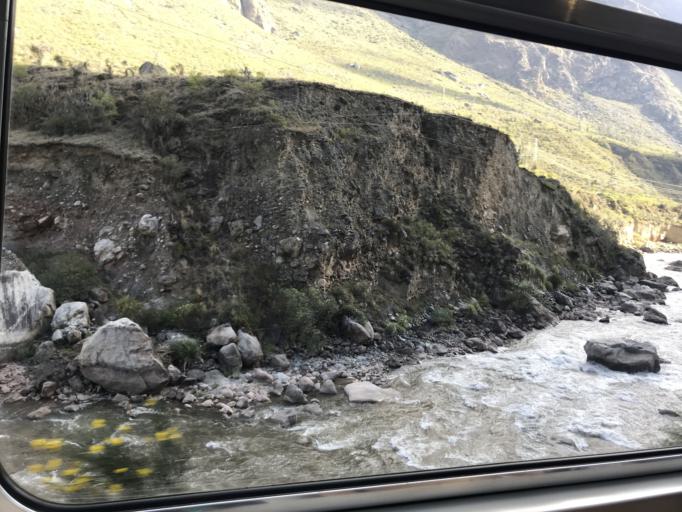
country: PE
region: Cusco
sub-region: Provincia de Urubamba
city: Ollantaytambo
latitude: -13.2212
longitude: -72.3942
